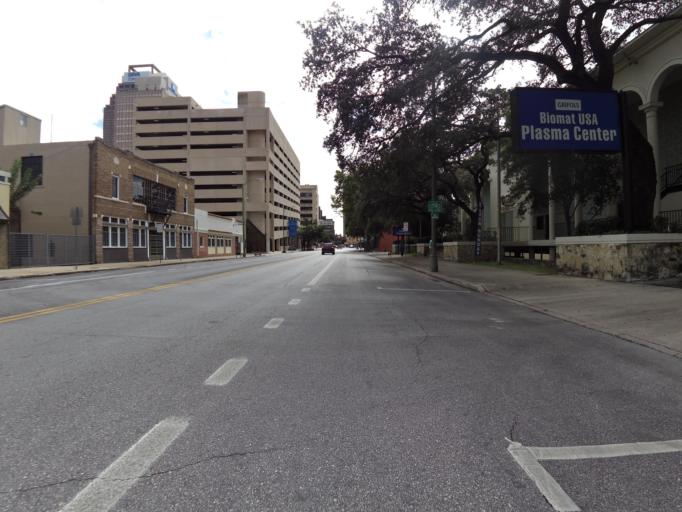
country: US
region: Texas
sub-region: Bexar County
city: San Antonio
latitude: 29.4306
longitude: -98.4940
